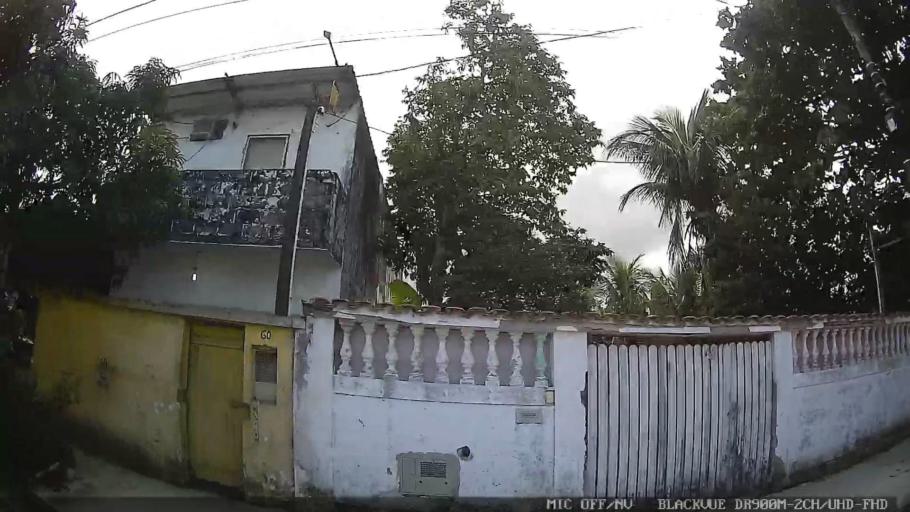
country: BR
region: Sao Paulo
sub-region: Guaruja
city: Guaruja
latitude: -23.9922
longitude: -46.2889
